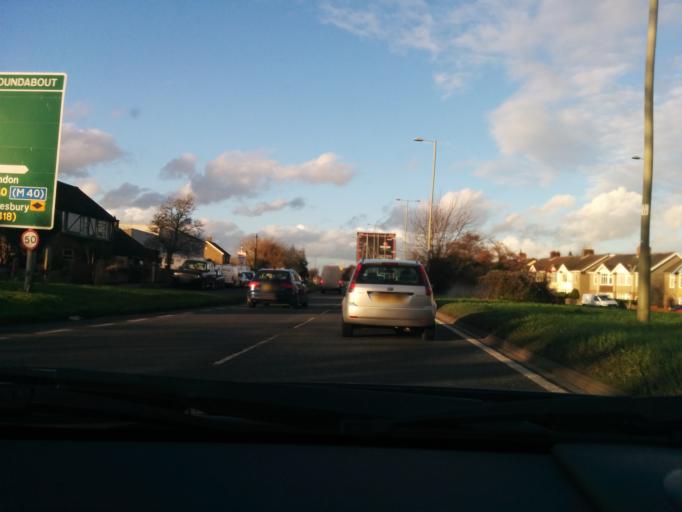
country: GB
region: England
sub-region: Oxfordshire
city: Cowley
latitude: 51.7598
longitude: -1.1951
